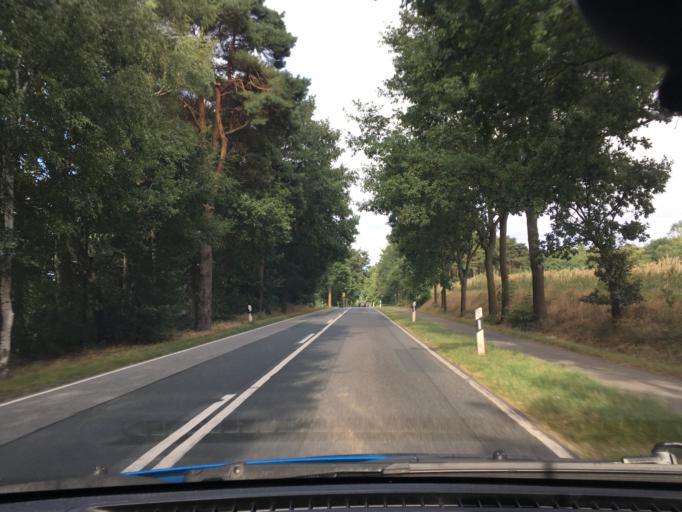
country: DE
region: Lower Saxony
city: Appel
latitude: 53.4069
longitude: 9.7942
